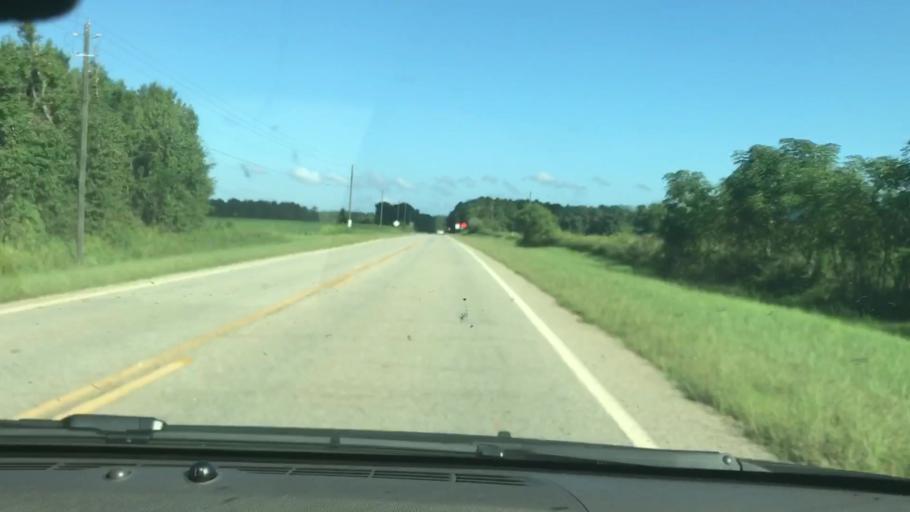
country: US
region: Georgia
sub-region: Clay County
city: Fort Gaines
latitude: 31.7374
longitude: -85.0492
